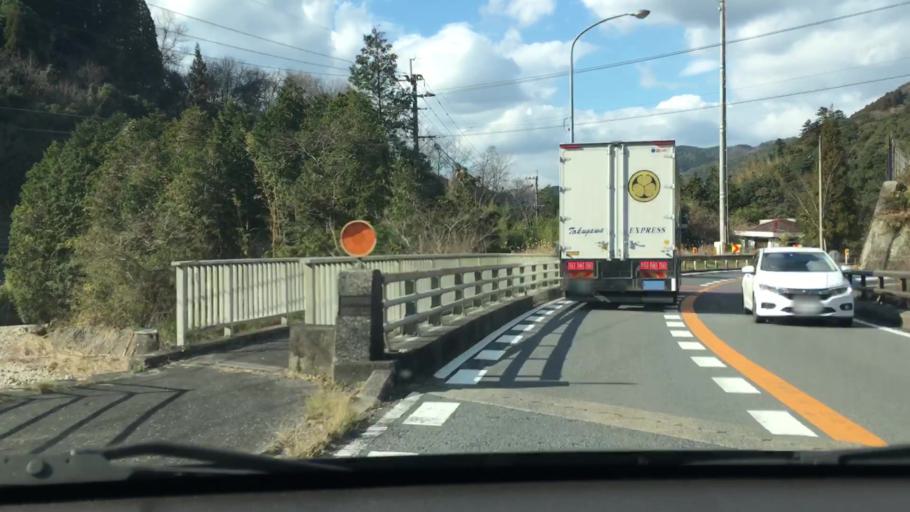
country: JP
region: Oita
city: Usuki
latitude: 32.9983
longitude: 131.7522
